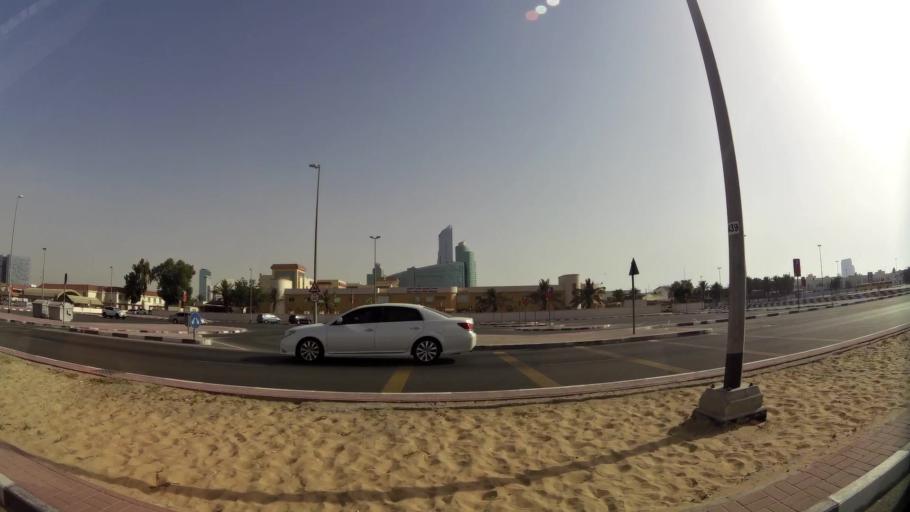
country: AE
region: Ash Shariqah
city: Sharjah
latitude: 25.2378
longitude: 55.3501
